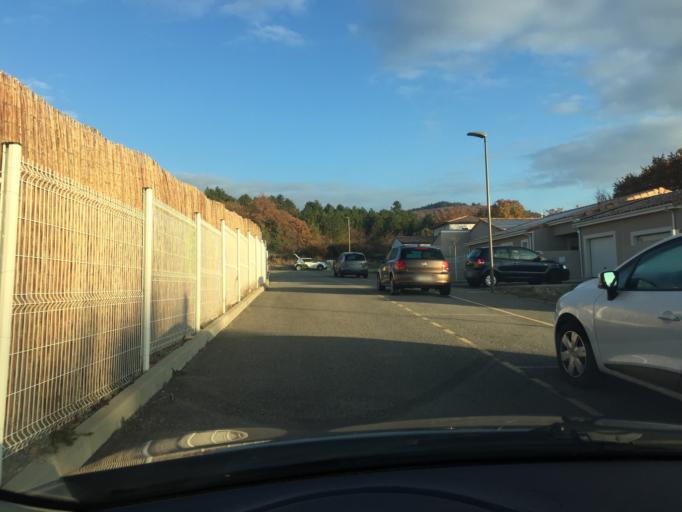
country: FR
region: Rhone-Alpes
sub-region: Departement de la Drome
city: Donzere
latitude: 44.4551
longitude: 4.7217
